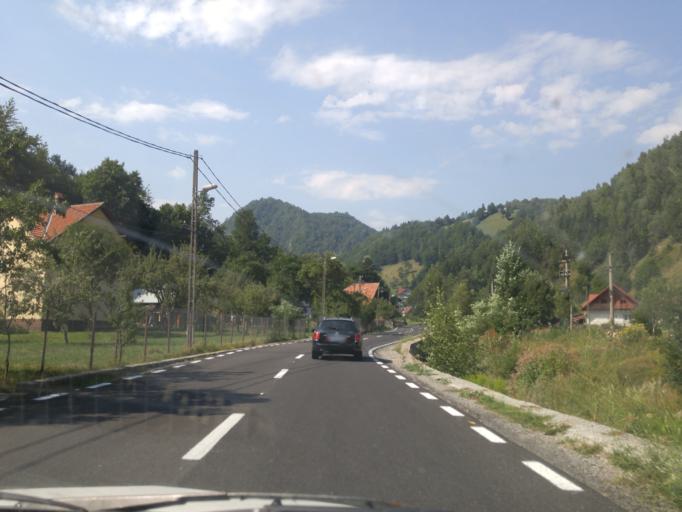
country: RO
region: Brasov
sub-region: Municipiul Brasov
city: Moeciu de Jos
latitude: 45.4784
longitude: 25.3139
